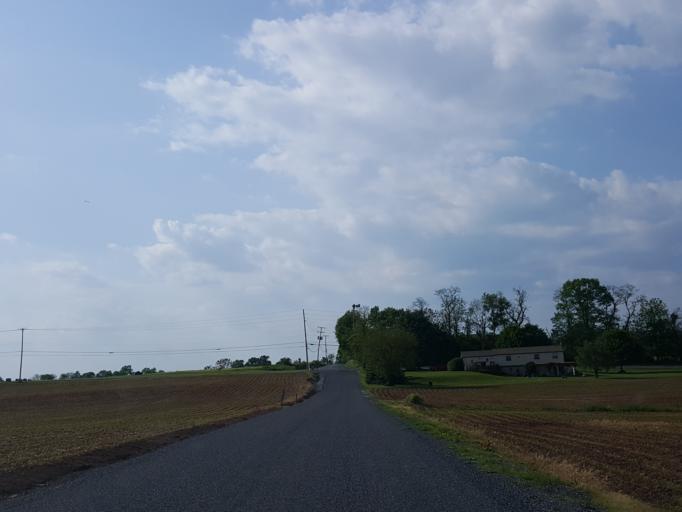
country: US
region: Pennsylvania
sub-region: Lebanon County
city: Campbelltown
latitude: 40.2263
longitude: -76.5766
